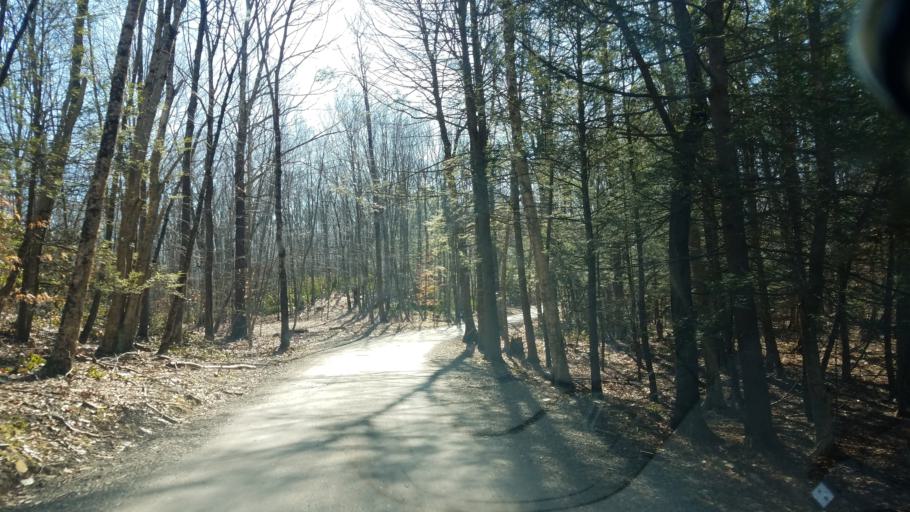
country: US
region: Connecticut
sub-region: New Haven County
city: Heritage Village
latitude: 41.5141
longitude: -73.2837
